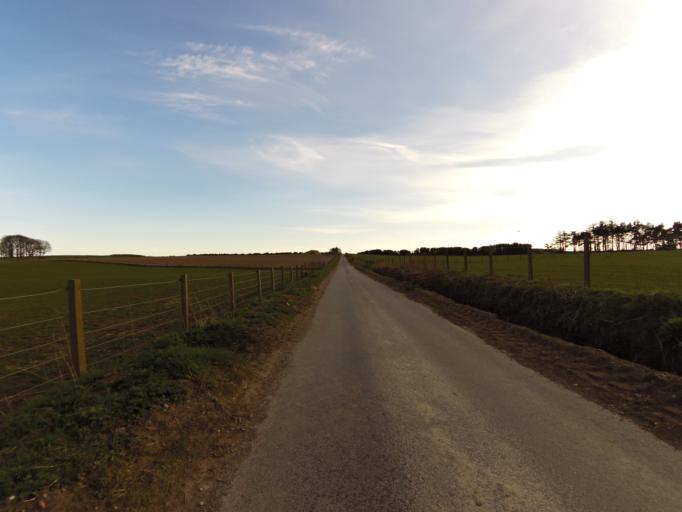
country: GB
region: Scotland
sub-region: Aberdeenshire
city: Stonehaven
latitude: 56.9421
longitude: -2.2210
